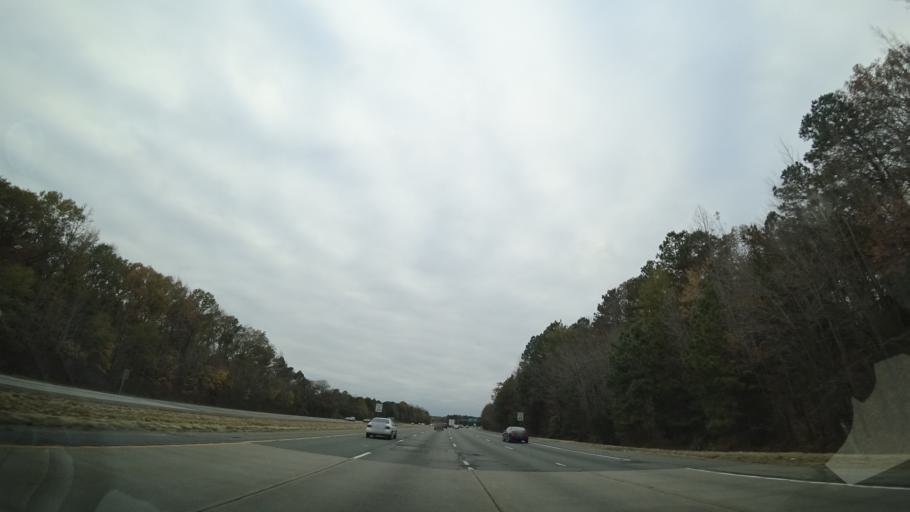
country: US
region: Virginia
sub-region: Henrico County
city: Chamberlayne
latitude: 37.6362
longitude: -77.3977
